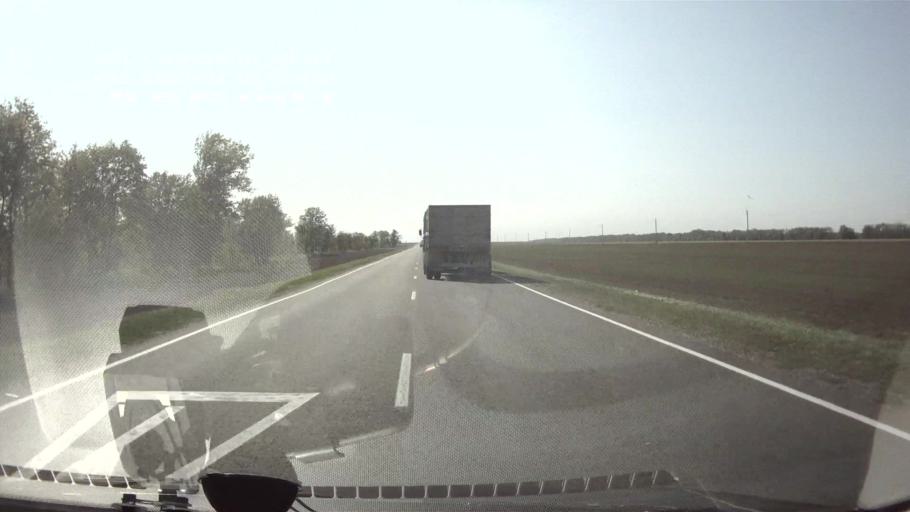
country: RU
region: Krasnodarskiy
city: Novopokrovskaya
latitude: 45.9050
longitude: 40.7212
